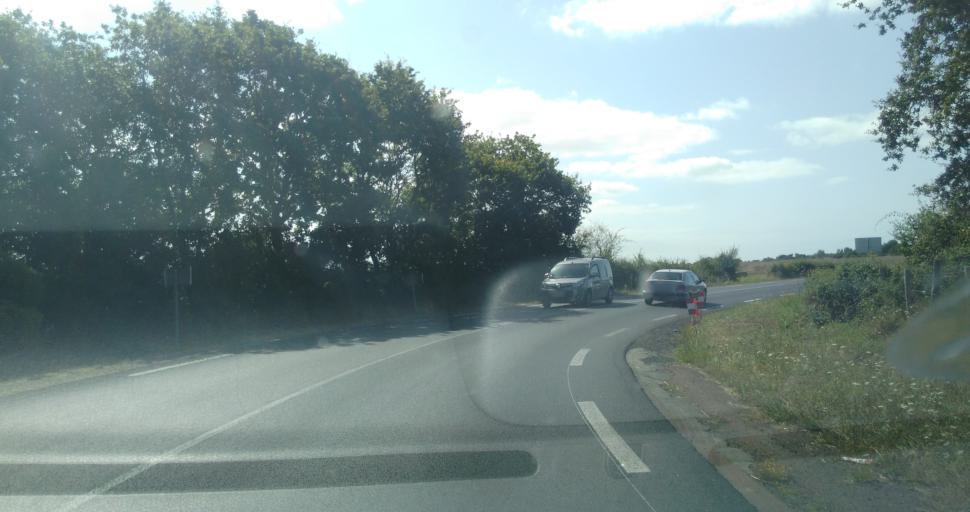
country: FR
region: Pays de la Loire
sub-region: Departement de la Vendee
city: Saint-Hilaire-de-Talmont
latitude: 46.4735
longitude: -1.6484
